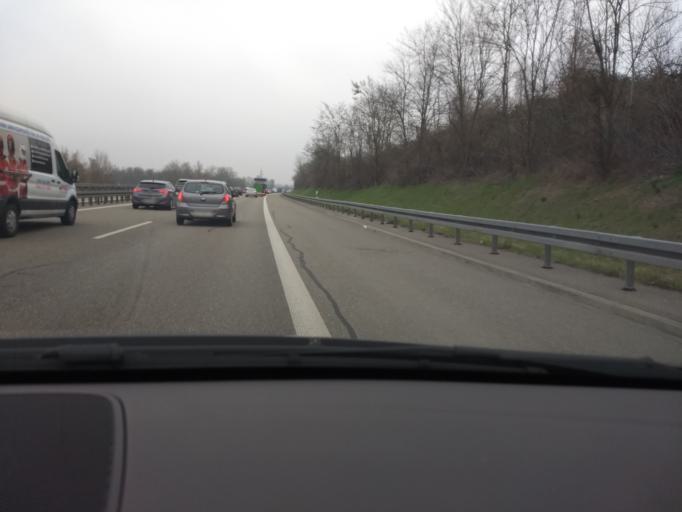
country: FR
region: Alsace
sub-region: Departement du Haut-Rhin
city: Kembs
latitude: 47.6901
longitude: 7.5209
